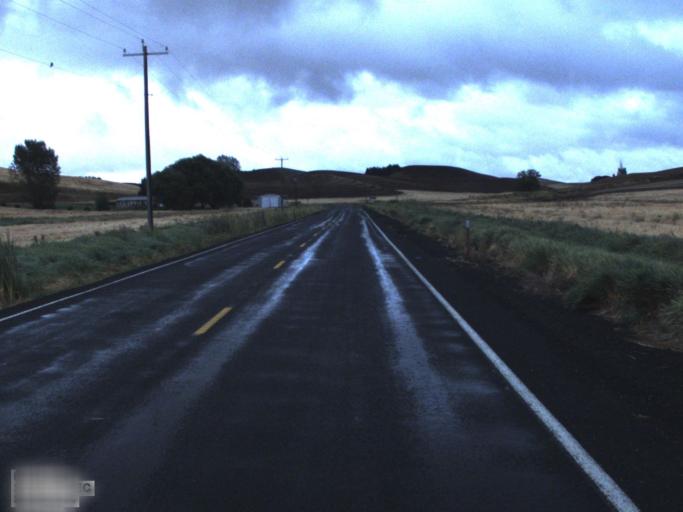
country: US
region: Washington
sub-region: Whitman County
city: Colfax
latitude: 47.0014
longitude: -117.4217
